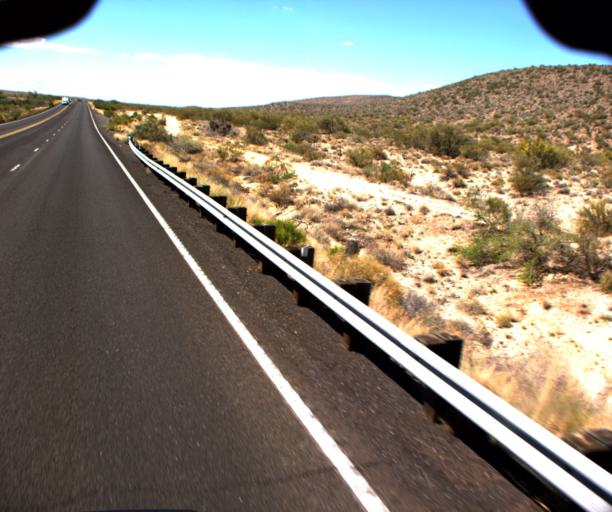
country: US
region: Arizona
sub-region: Mohave County
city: Kingman
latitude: 34.9362
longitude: -113.6624
